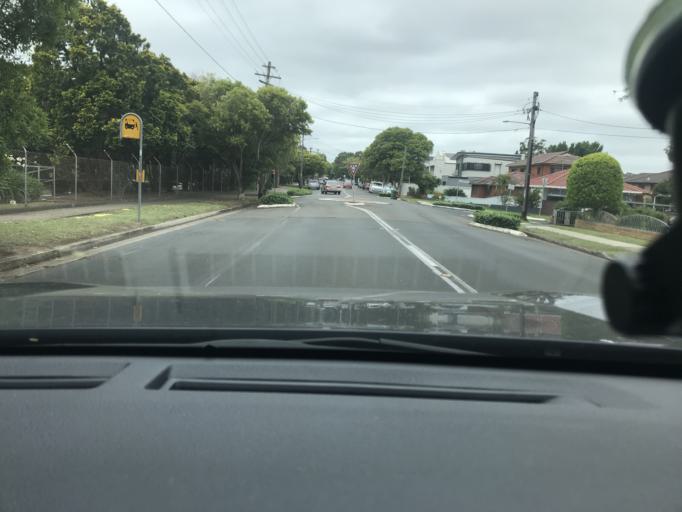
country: AU
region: New South Wales
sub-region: Canada Bay
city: Wareemba
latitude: -33.8588
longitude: 151.1158
